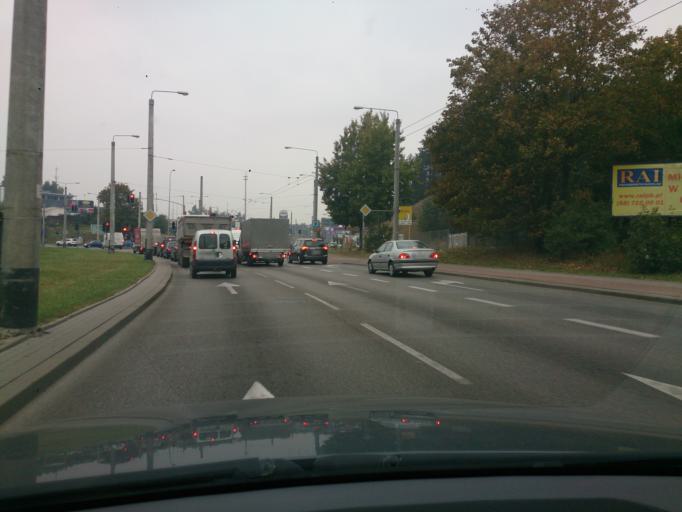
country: PL
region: Pomeranian Voivodeship
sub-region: Gdynia
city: Wielki Kack
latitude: 54.4720
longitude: 18.4824
